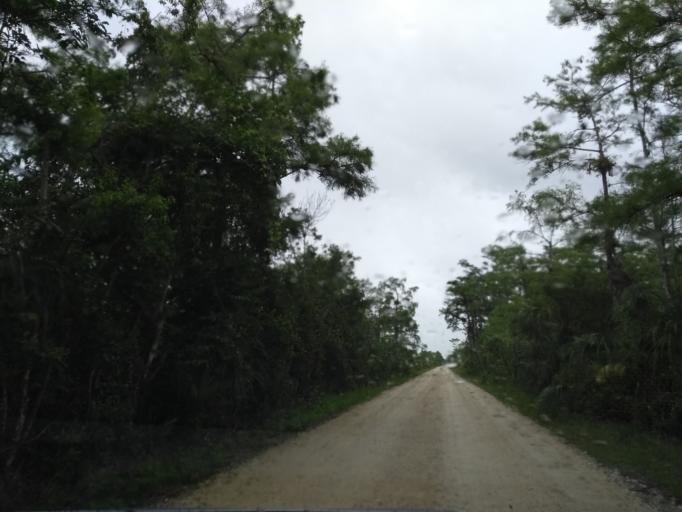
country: US
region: Florida
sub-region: Miami-Dade County
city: The Hammocks
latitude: 25.7603
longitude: -81.0117
